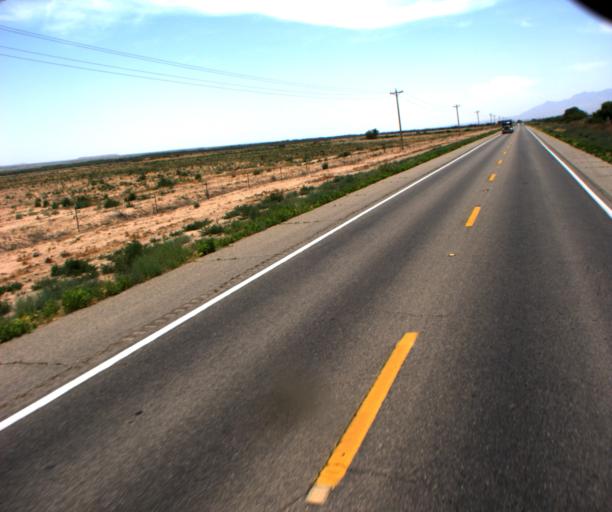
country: US
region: Arizona
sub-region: Graham County
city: Pima
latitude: 33.0088
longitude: -109.9480
